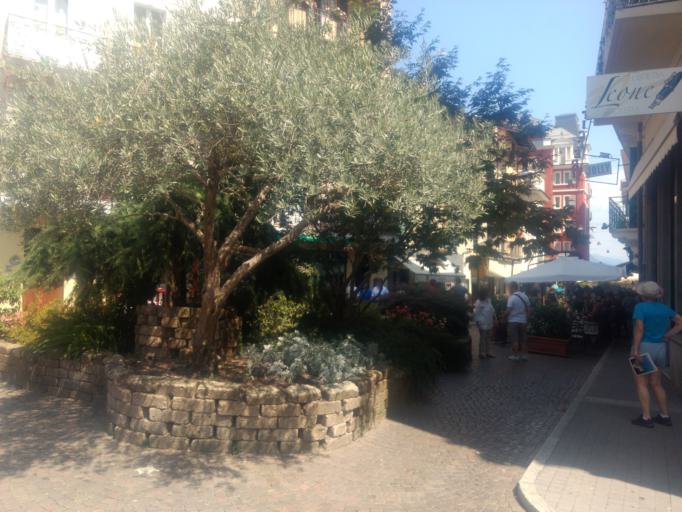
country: IT
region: Piedmont
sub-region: Provincia Verbano-Cusio-Ossola
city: Stresa
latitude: 45.8836
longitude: 8.5397
